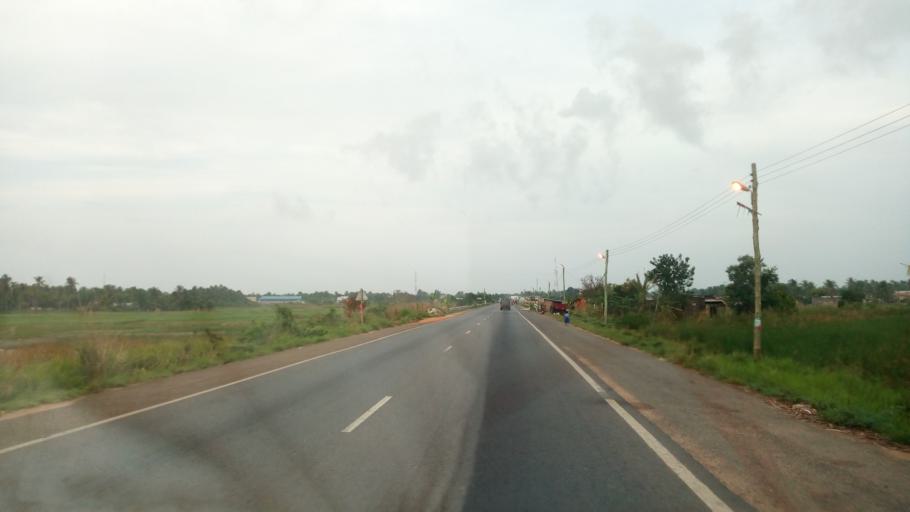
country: GH
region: Volta
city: Keta
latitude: 6.0787
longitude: 1.0449
